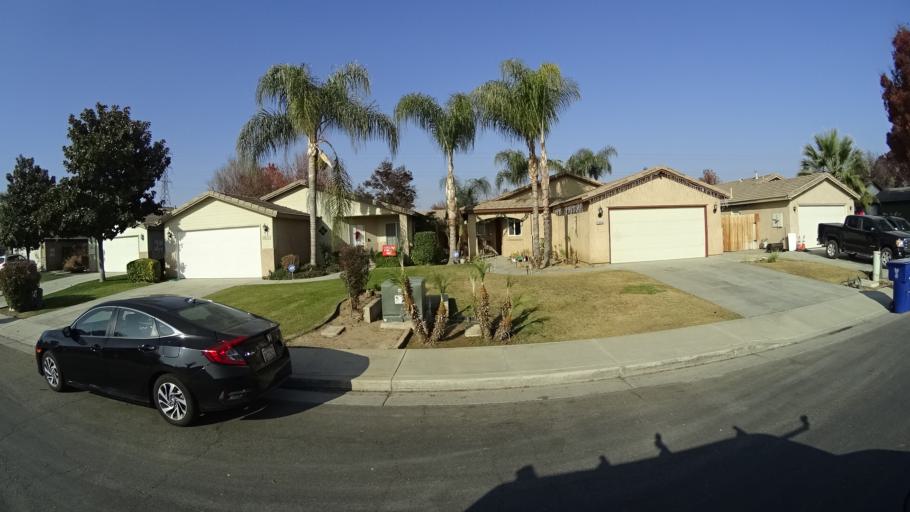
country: US
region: California
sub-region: Kern County
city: Greenacres
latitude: 35.3962
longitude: -119.0683
